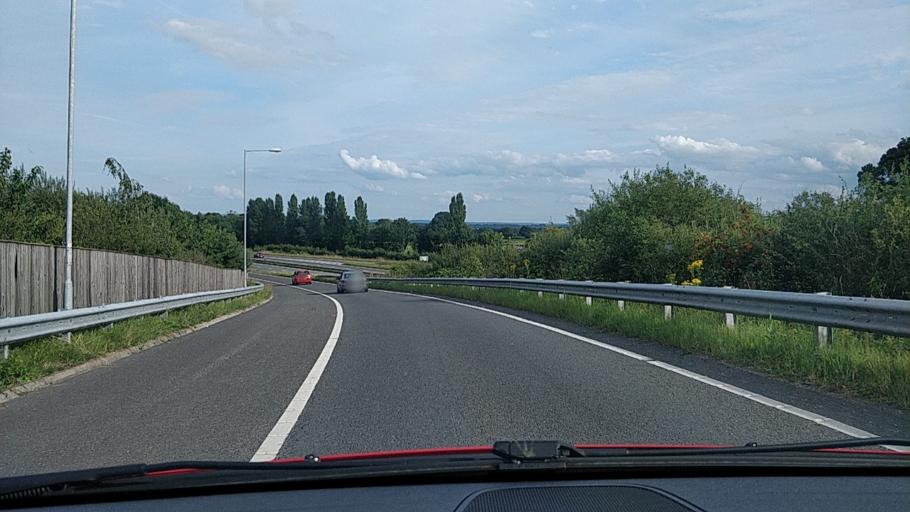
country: GB
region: Wales
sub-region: County of Flintshire
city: Hawarden
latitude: 53.1614
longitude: -3.0056
